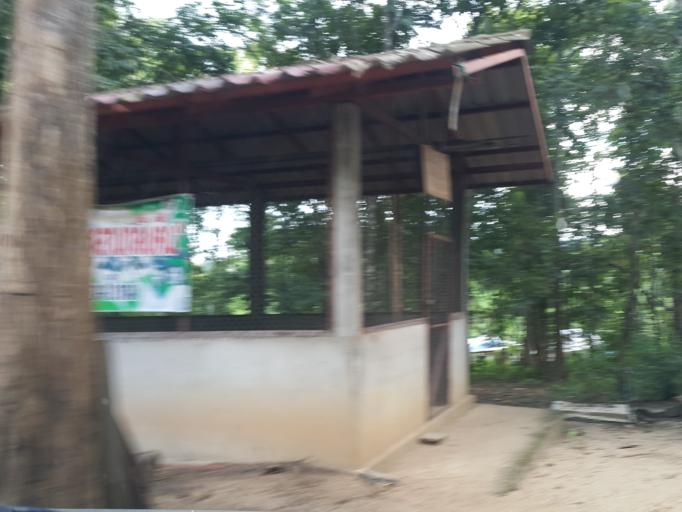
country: TH
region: Chiang Mai
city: Phrao
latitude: 19.3333
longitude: 99.1467
